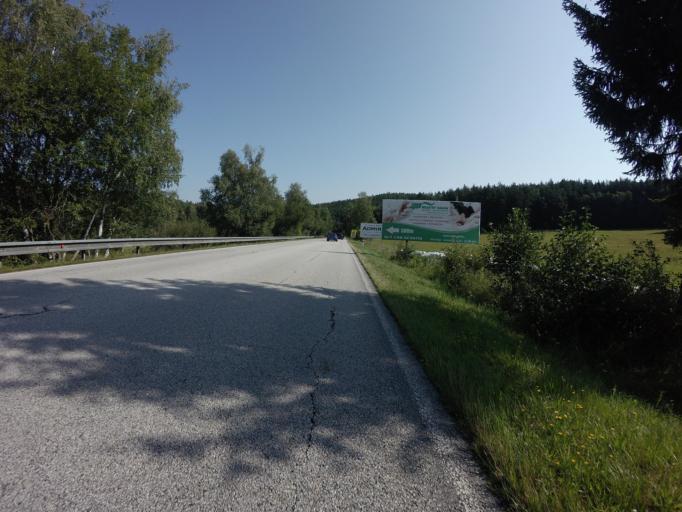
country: CZ
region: Jihocesky
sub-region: Okres Cesky Krumlov
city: Vyssi Brod
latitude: 48.5707
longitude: 14.3196
